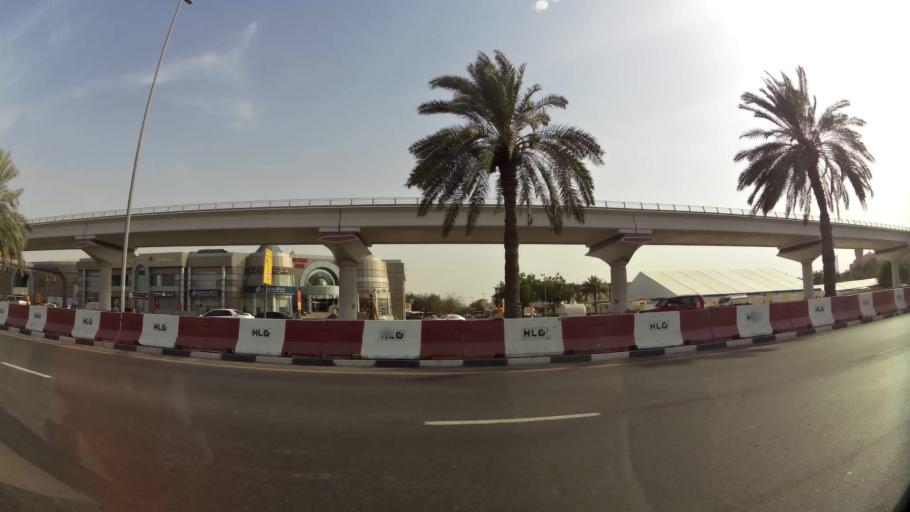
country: AE
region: Ash Shariqah
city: Sharjah
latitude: 25.2340
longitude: 55.3842
